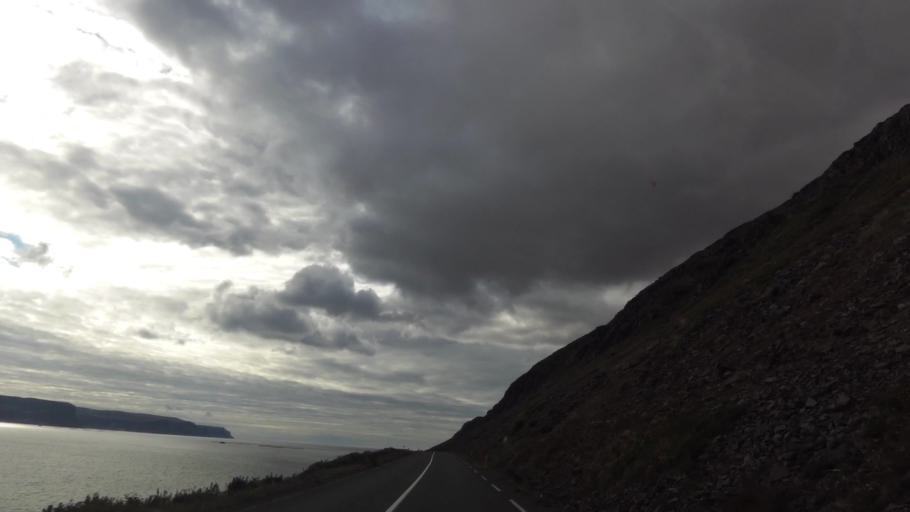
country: IS
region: West
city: Olafsvik
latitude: 65.5673
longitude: -23.9245
